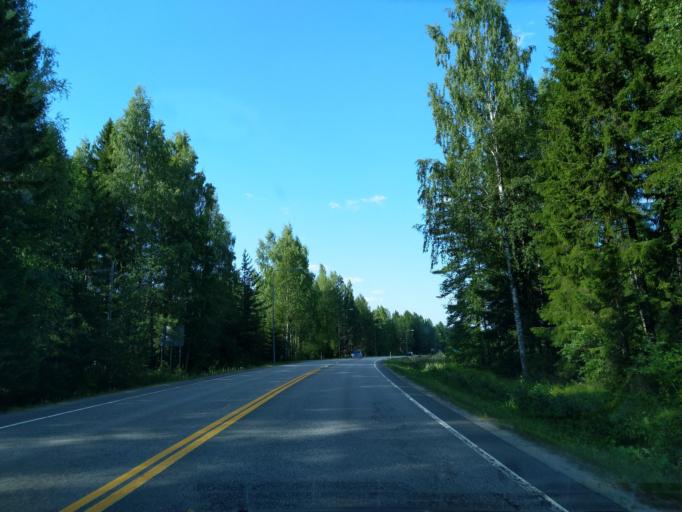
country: FI
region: Pirkanmaa
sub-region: Luoteis-Pirkanmaa
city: Kihnioe
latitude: 62.1935
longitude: 23.1712
